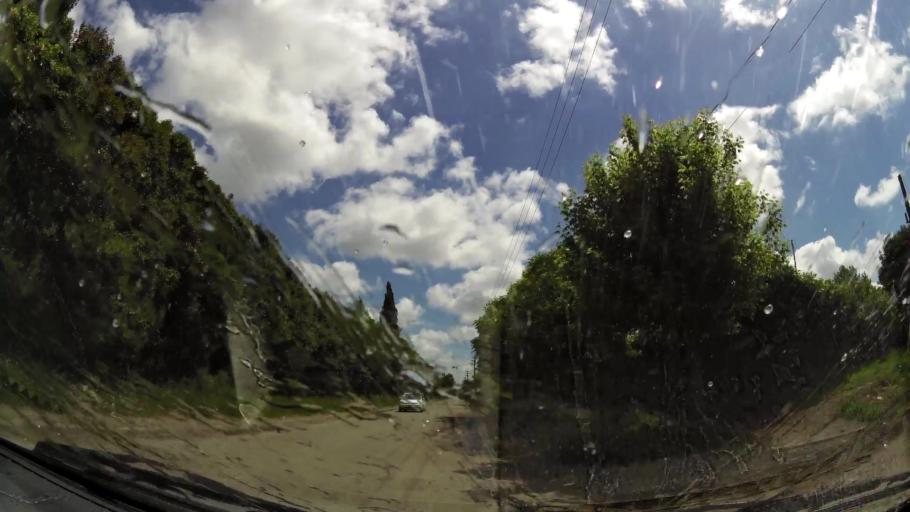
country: AR
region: Buenos Aires
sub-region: Partido de Quilmes
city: Quilmes
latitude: -34.8432
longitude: -58.2336
